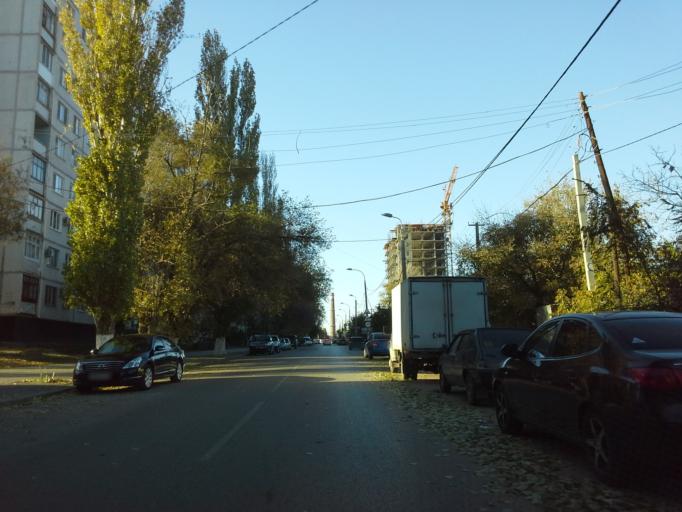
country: RU
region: Volgograd
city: Vodstroy
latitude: 48.8168
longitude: 44.6366
